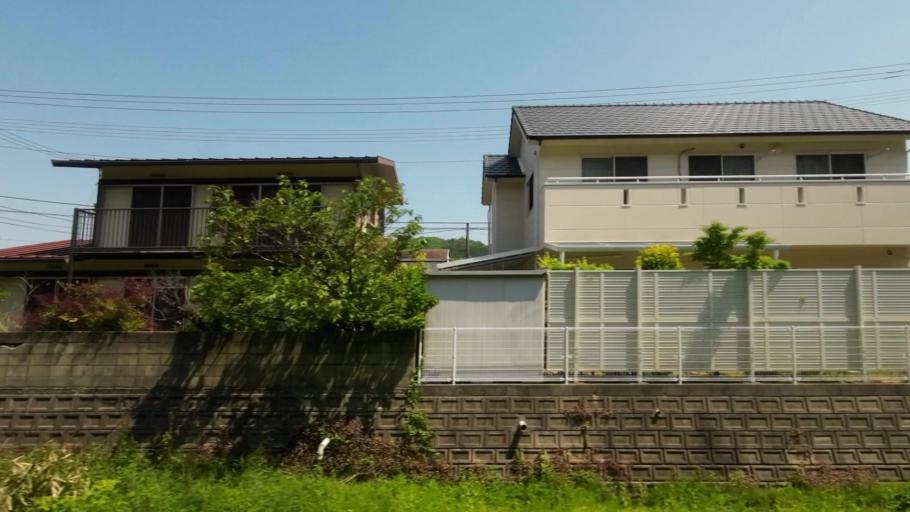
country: JP
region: Ehime
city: Hojo
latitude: 34.0972
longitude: 132.9508
